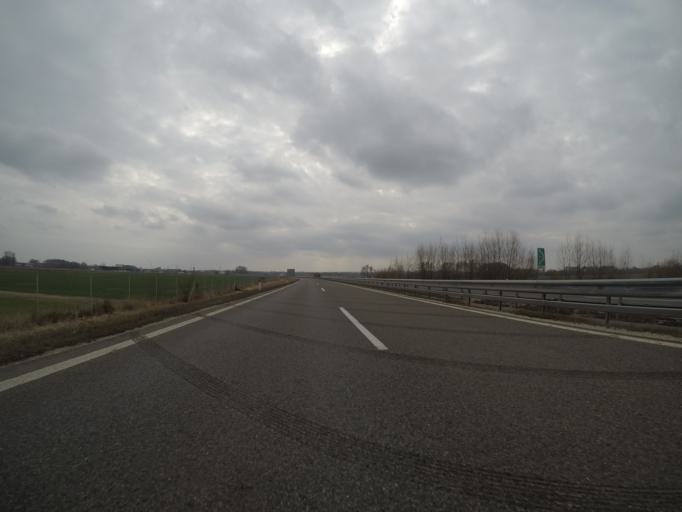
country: SI
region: Lendava-Lendva
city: Lendava
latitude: 46.5467
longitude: 16.4426
